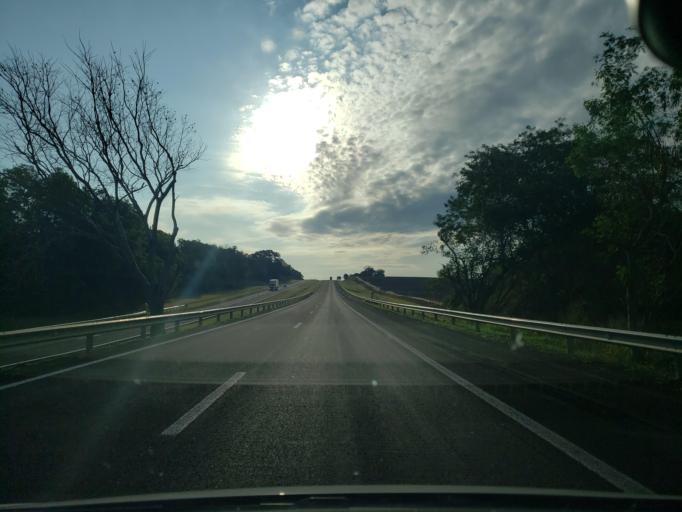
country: BR
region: Sao Paulo
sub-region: Valparaiso
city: Valparaiso
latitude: -21.1860
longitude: -50.9139
